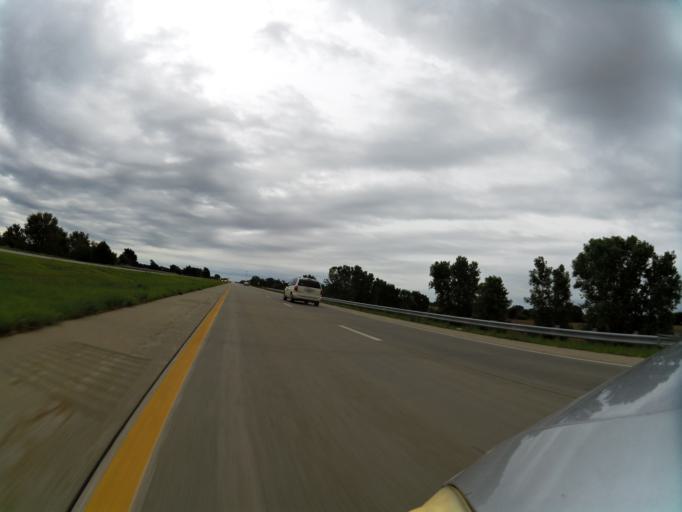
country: US
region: Kansas
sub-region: Reno County
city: Haven
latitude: 37.9226
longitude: -97.8350
